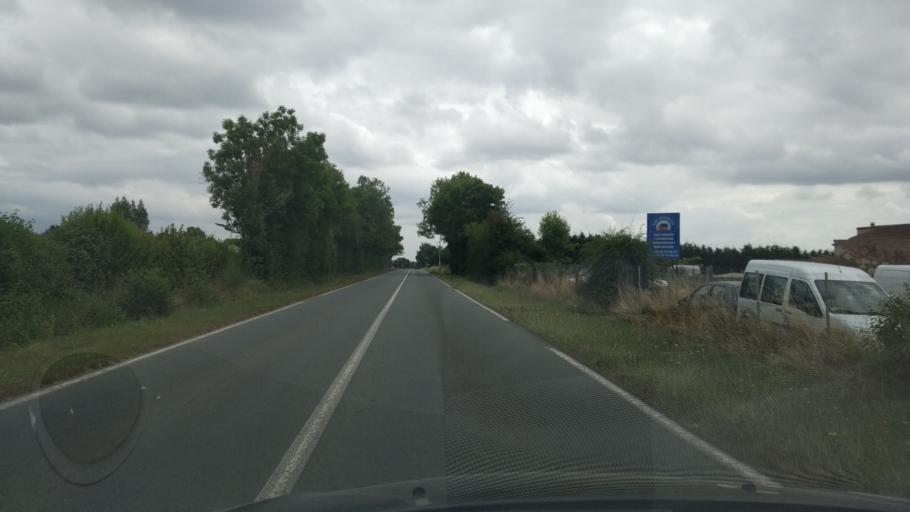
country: FR
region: Poitou-Charentes
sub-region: Departement de la Vienne
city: Roches-Premarie-Andille
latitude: 46.4932
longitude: 0.3666
